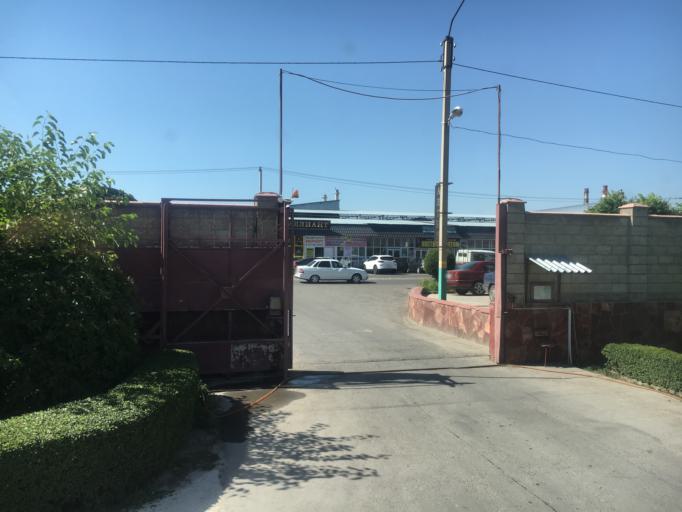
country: KZ
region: Zhambyl
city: Taraz
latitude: 42.9092
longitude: 71.4116
